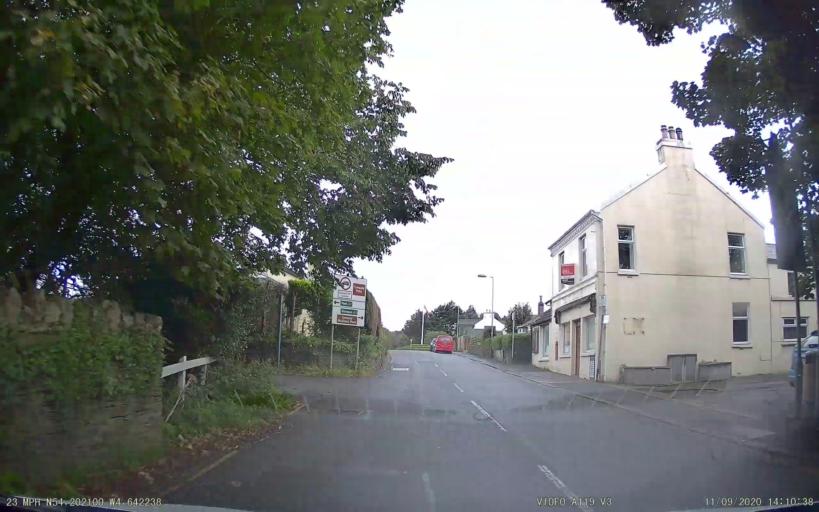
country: IM
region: Castletown
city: Castletown
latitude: 54.2021
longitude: -4.6422
